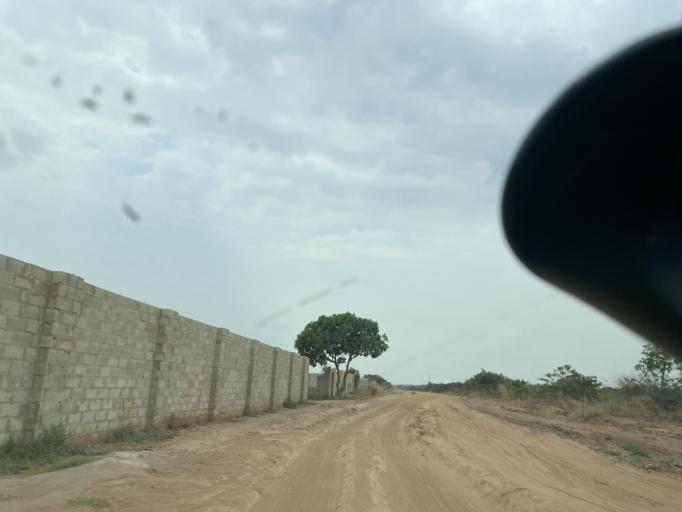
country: ZM
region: Lusaka
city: Lusaka
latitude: -15.2149
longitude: 28.3385
